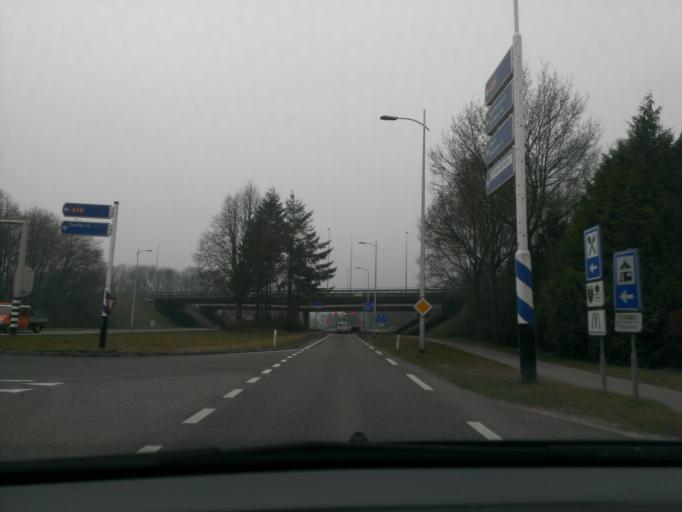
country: NL
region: Gelderland
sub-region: Gemeente Heerde
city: Heerde
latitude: 52.3739
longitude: 6.0239
